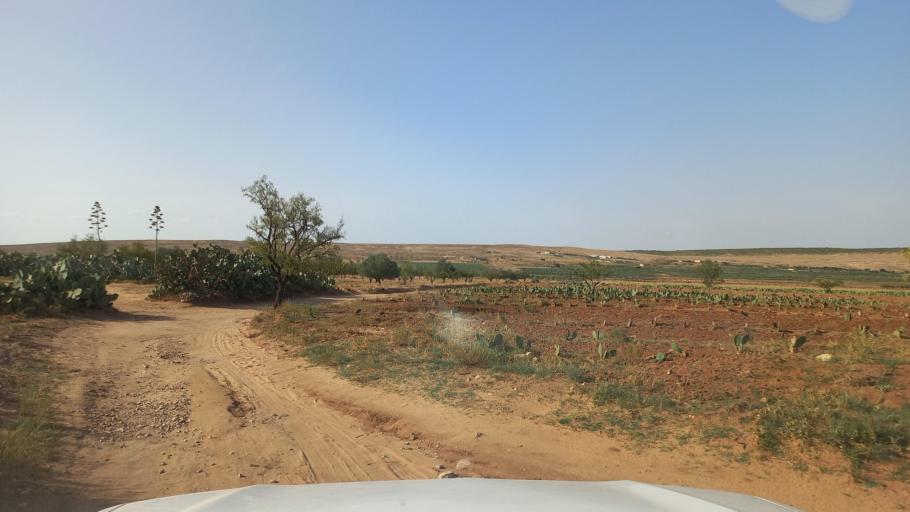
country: TN
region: Al Qasrayn
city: Kasserine
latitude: 35.3502
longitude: 8.8487
